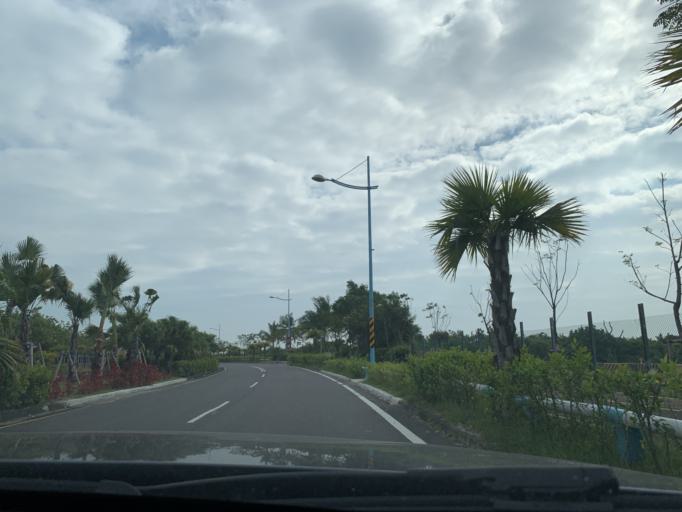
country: TW
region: Taiwan
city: Fengshan
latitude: 22.4452
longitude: 120.4877
